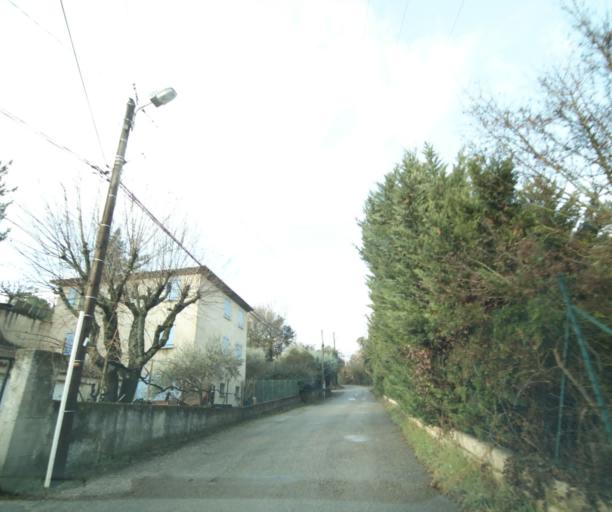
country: FR
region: Provence-Alpes-Cote d'Azur
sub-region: Departement du Var
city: Tourves
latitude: 43.4057
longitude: 5.9183
